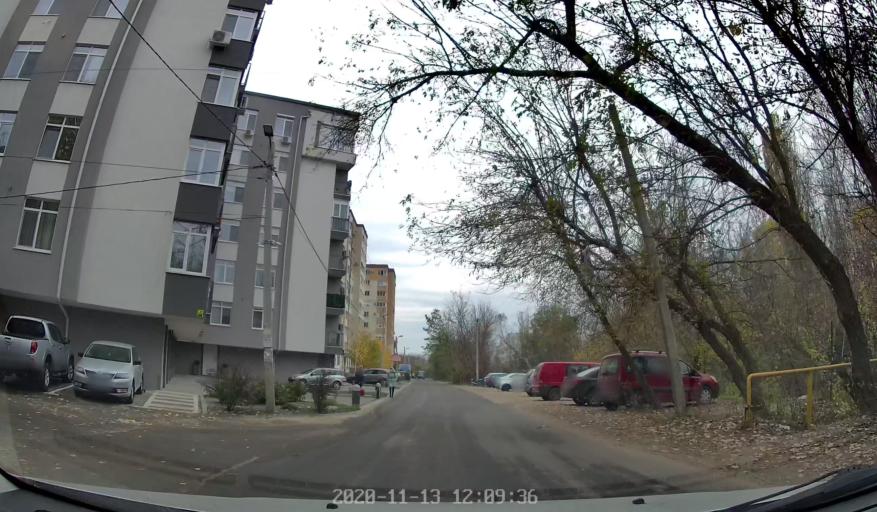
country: MD
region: Chisinau
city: Chisinau
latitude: 46.9584
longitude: 28.8365
